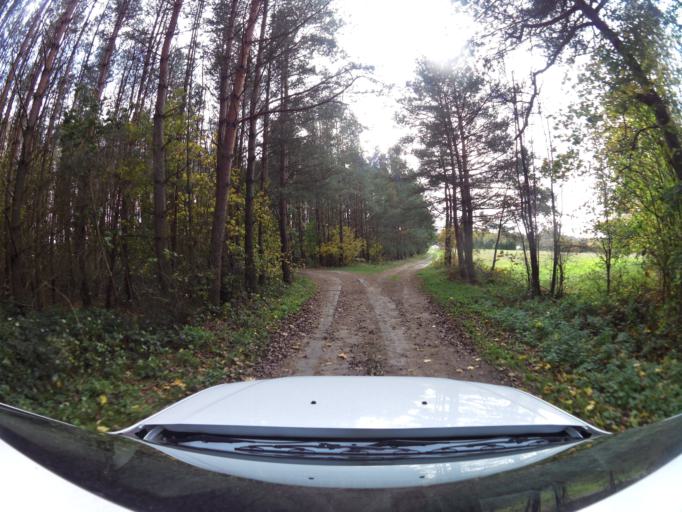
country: PL
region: West Pomeranian Voivodeship
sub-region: Powiat gryficki
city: Gryfice
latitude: 53.8718
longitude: 15.1211
